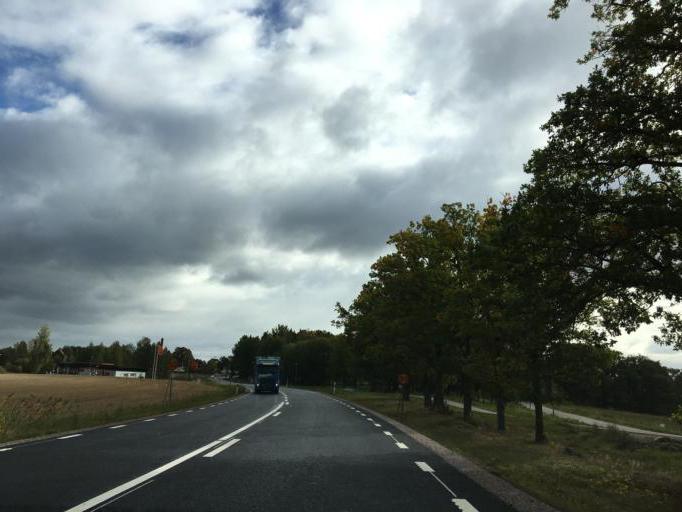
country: SE
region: Soedermanland
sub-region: Nykopings Kommun
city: Olstorp
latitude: 58.8635
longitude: 16.6923
